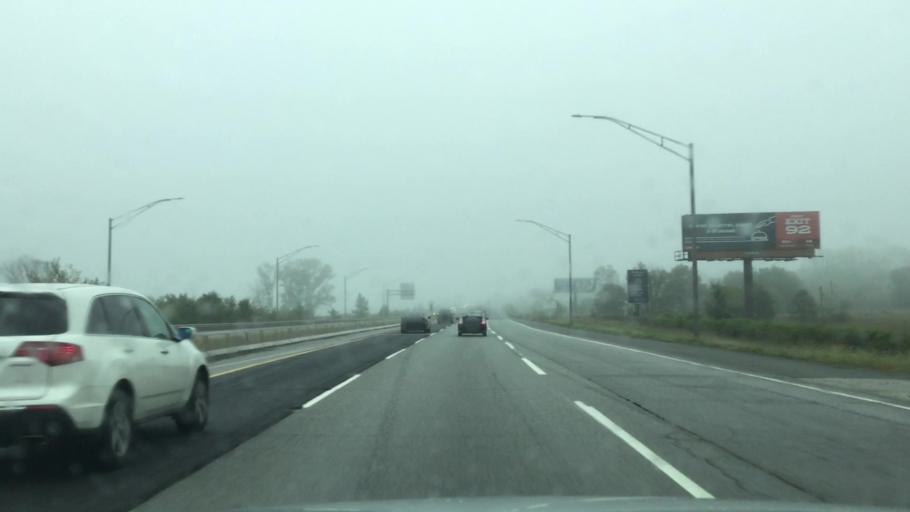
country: US
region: Indiana
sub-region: Lake County
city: East Chicago
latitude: 41.6088
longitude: -87.4147
